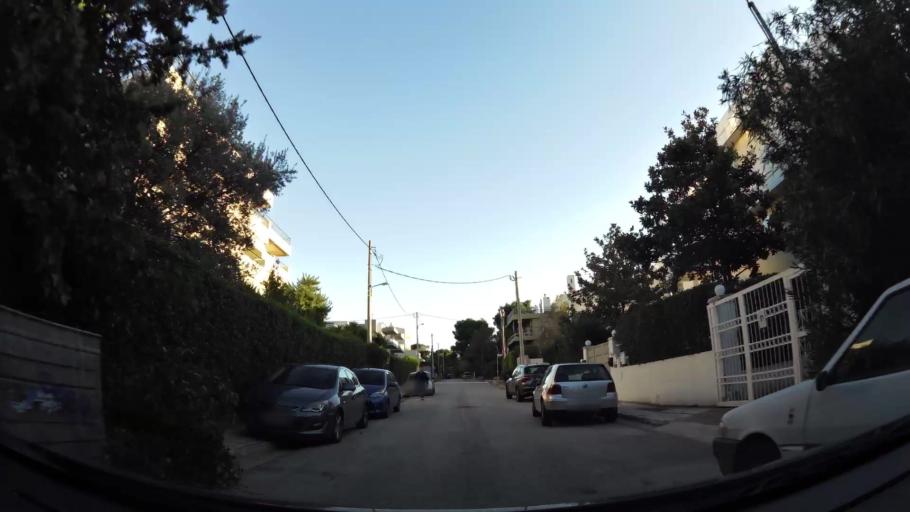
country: GR
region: Attica
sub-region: Nomarchia Athinas
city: Kifisia
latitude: 38.0829
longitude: 23.8240
